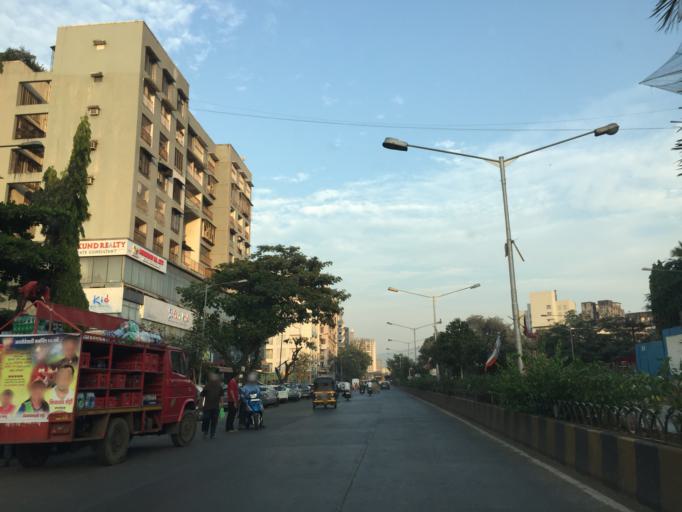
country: IN
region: Maharashtra
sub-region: Mumbai Suburban
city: Borivli
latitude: 19.2205
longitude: 72.8495
